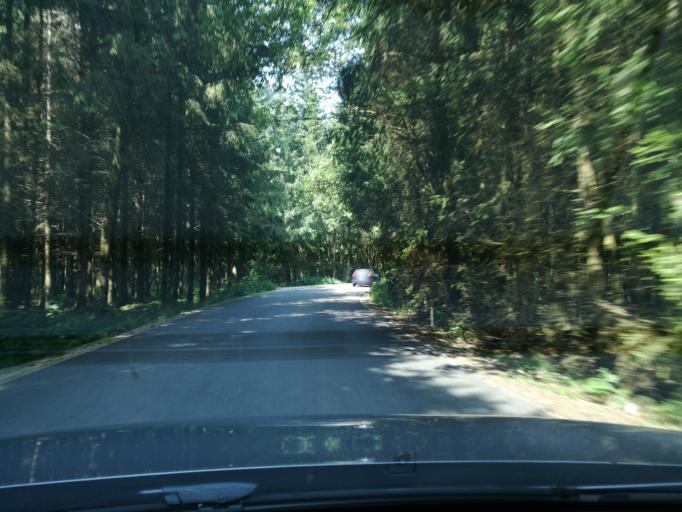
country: AT
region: Upper Austria
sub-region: Politischer Bezirk Grieskirchen
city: Grieskirchen
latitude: 48.2984
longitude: 13.7963
